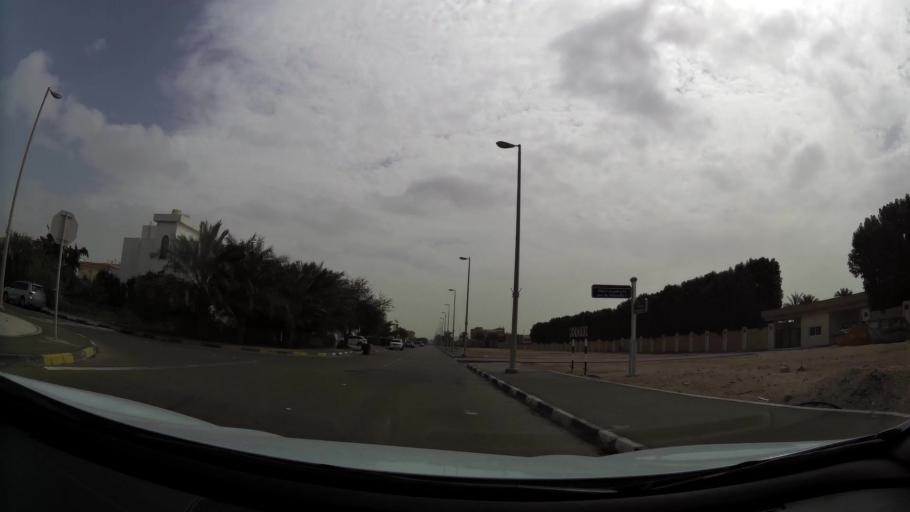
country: AE
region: Abu Dhabi
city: Abu Dhabi
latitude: 24.3951
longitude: 54.4891
